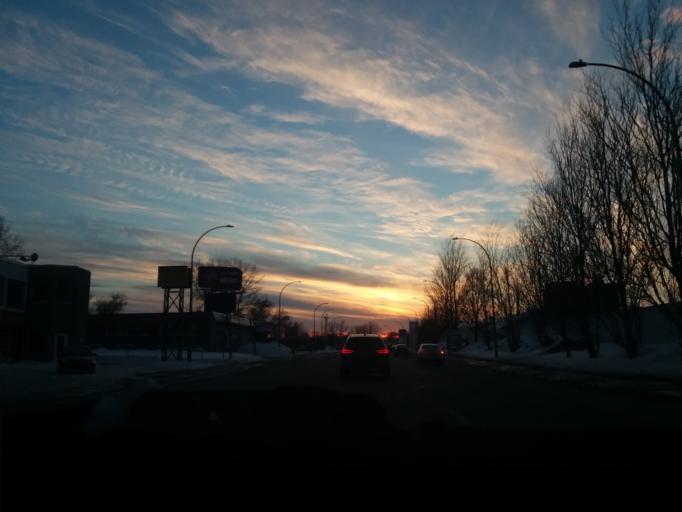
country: CA
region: Quebec
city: Saint-Raymond
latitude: 45.4629
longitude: -73.6196
